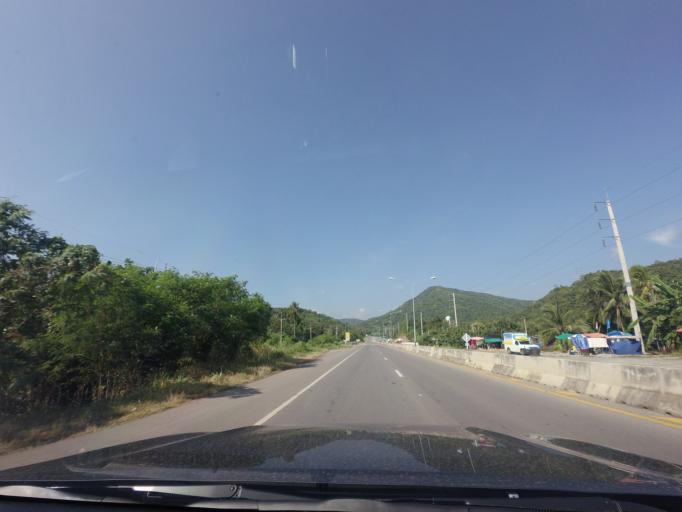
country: TH
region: Phetchabun
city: Lom Sak
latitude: 16.7640
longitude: 101.1504
